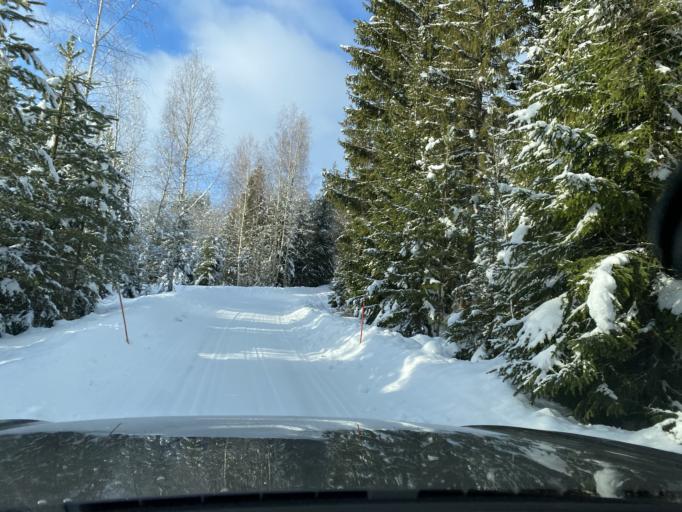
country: FI
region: Pirkanmaa
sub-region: Lounais-Pirkanmaa
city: Punkalaidun
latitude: 61.0716
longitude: 23.2381
